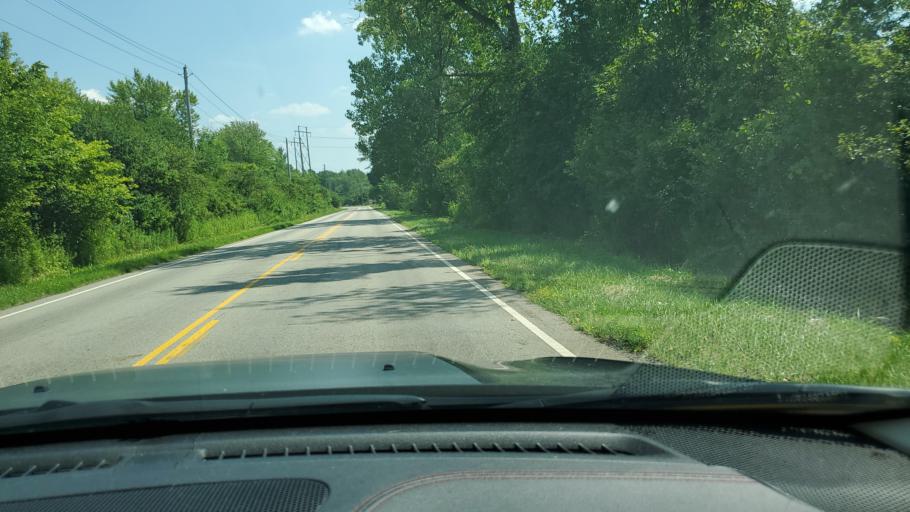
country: US
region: Ohio
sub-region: Trumbull County
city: Bolindale
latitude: 41.2077
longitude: -80.8018
